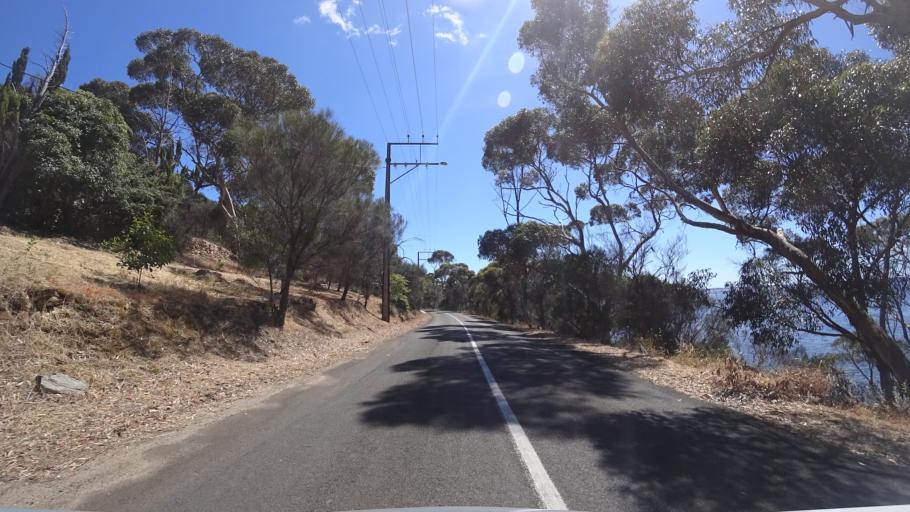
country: AU
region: South Australia
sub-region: Kangaroo Island
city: Kingscote
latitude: -35.7791
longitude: 137.7739
